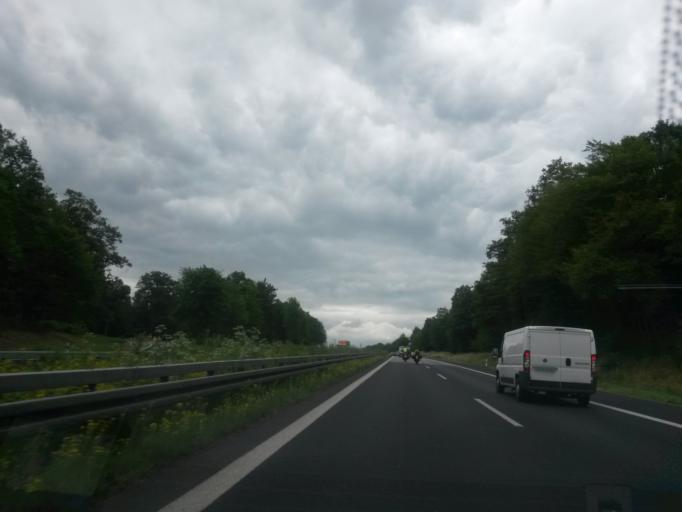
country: DE
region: Bavaria
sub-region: Regierungsbezirk Unterfranken
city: Rottendorf
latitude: 49.8175
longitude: 10.0431
